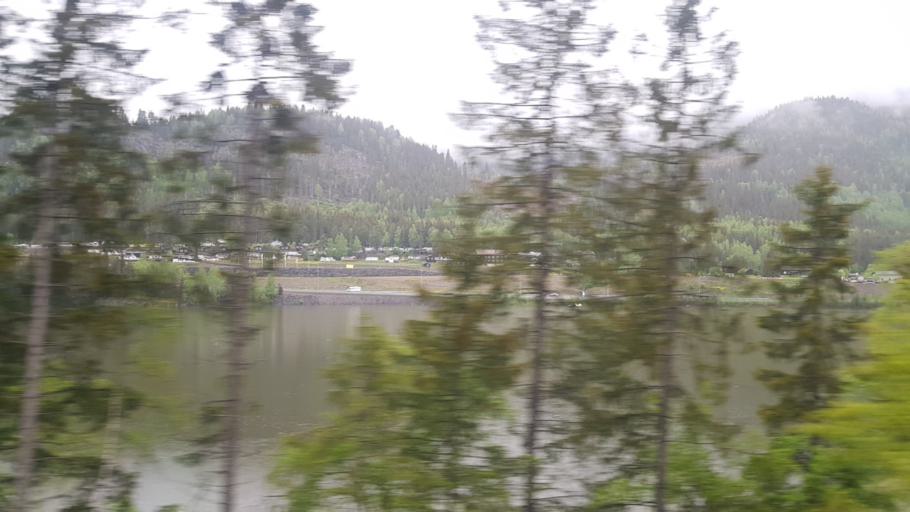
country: NO
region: Oppland
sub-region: Oyer
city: Tretten
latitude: 61.2691
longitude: 10.3924
